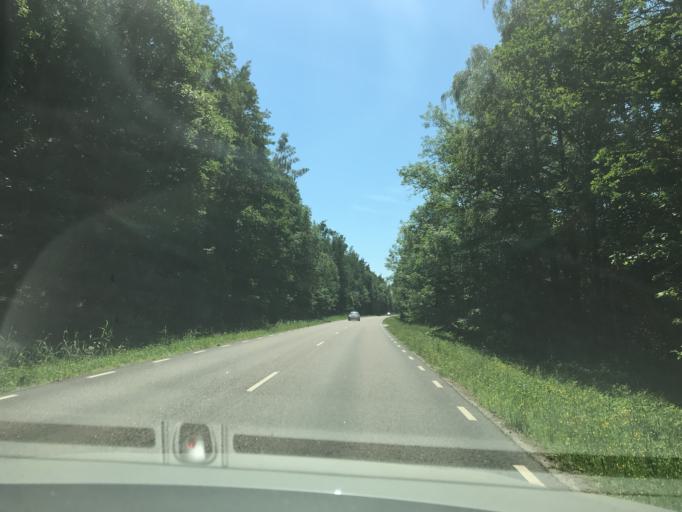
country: SE
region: Vaestra Goetaland
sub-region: Gotene Kommun
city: Kallby
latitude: 58.6040
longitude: 13.3969
